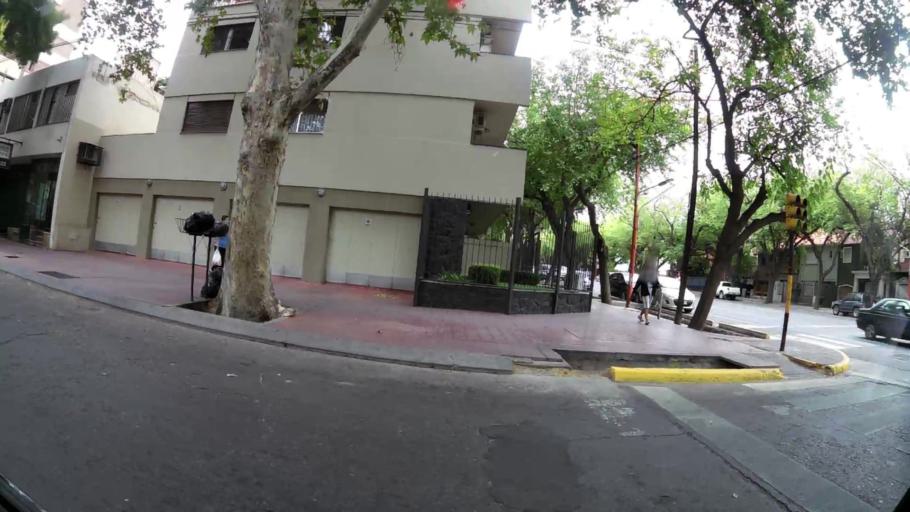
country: AR
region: Mendoza
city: Mendoza
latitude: -32.8881
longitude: -68.8539
